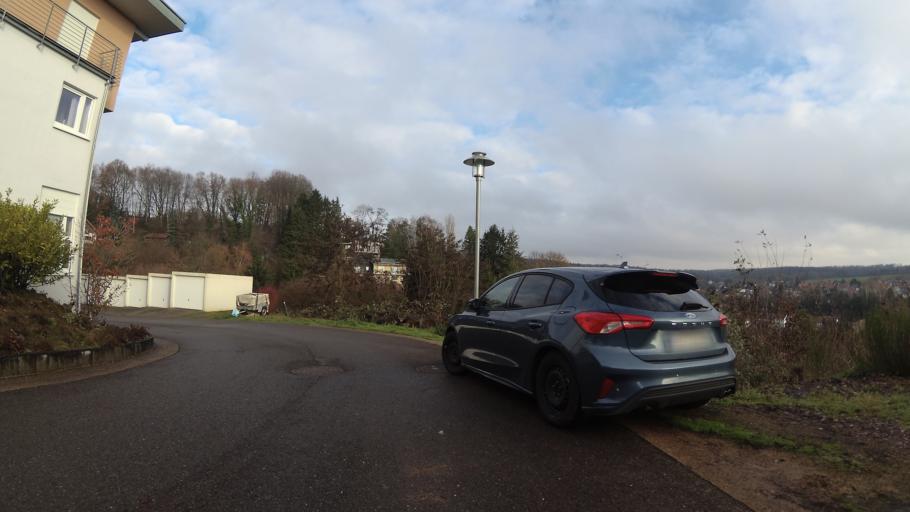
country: DE
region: Saarland
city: Spiesen-Elversberg
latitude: 49.3196
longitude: 7.1524
